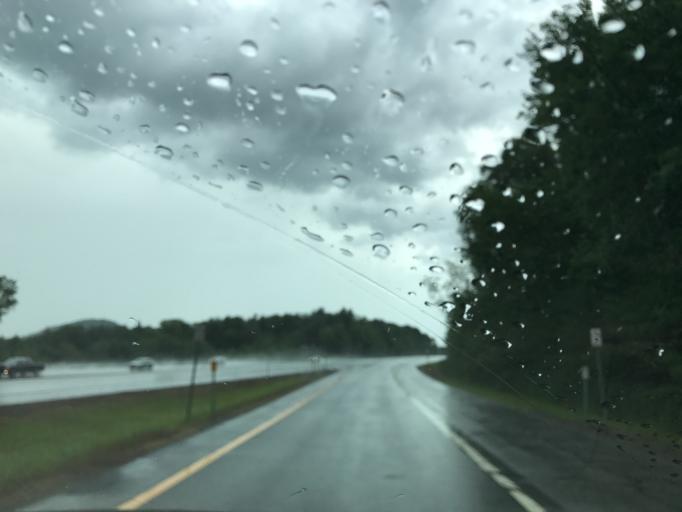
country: US
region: New York
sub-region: Warren County
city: Warrensburg
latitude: 43.4894
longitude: -73.7522
